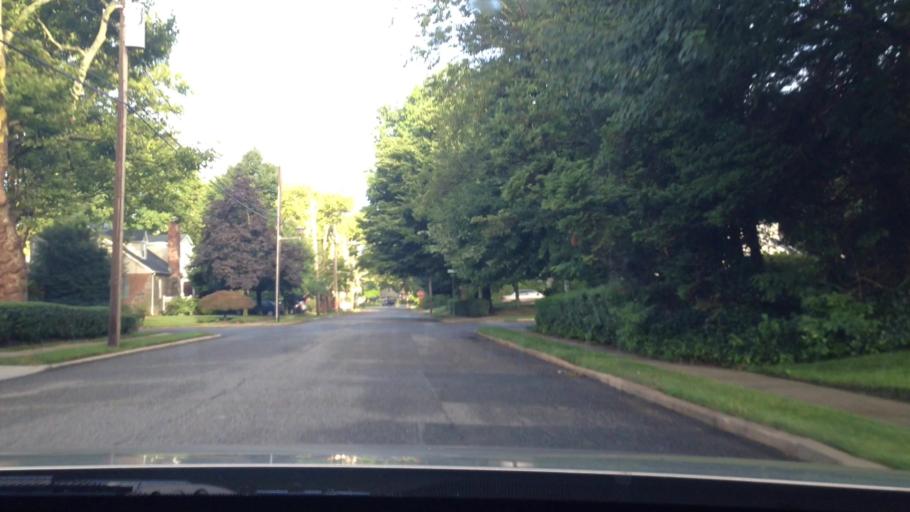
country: US
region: New York
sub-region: Nassau County
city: Stewart Manor
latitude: 40.7170
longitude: -73.6847
